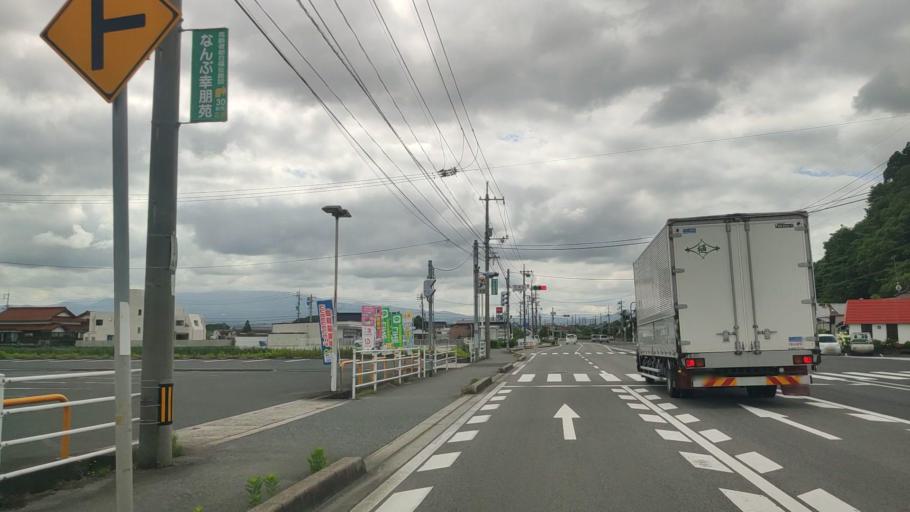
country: JP
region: Tottori
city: Yonago
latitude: 35.4112
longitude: 133.3581
